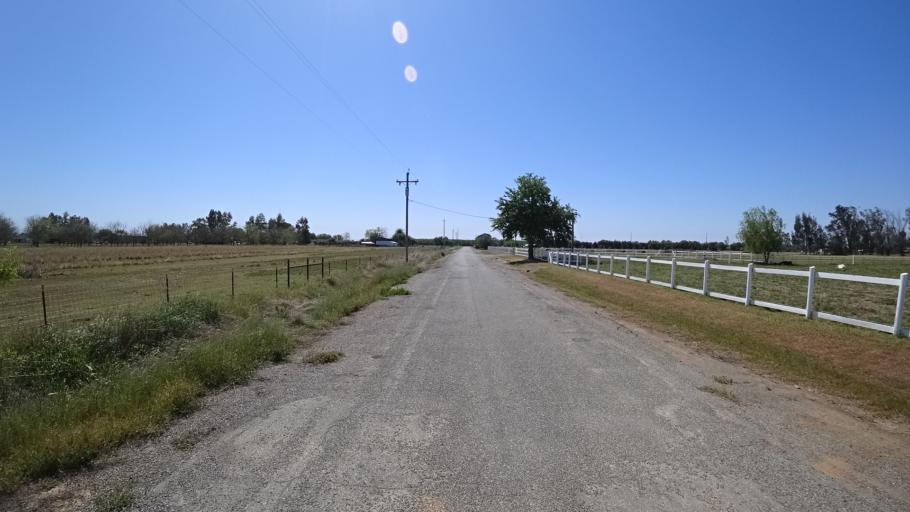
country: US
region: California
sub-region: Glenn County
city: Orland
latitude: 39.7722
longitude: -122.1829
